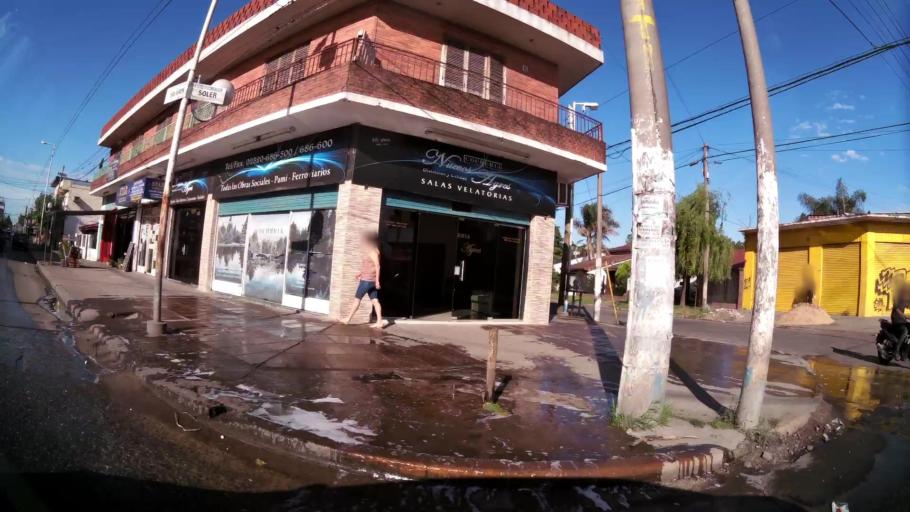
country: AR
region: Buenos Aires
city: Santa Catalina - Dique Lujan
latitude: -34.4926
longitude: -58.7274
